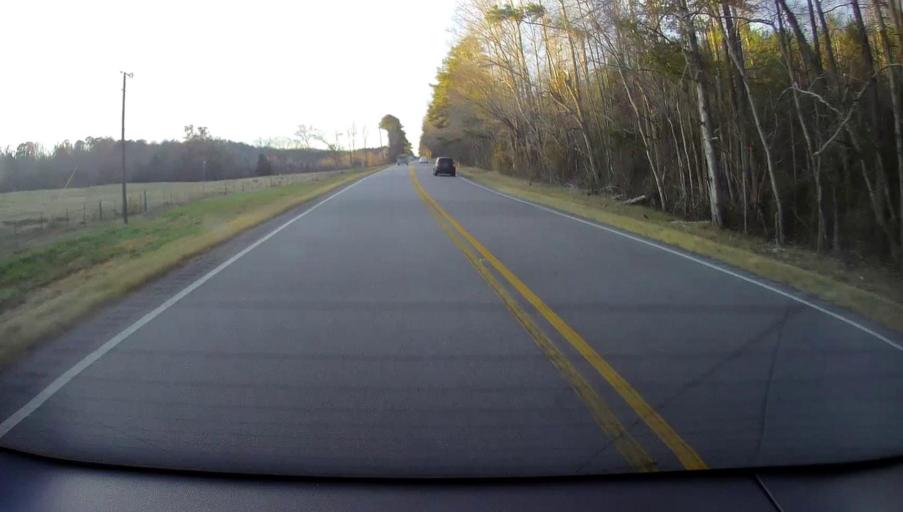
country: US
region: Alabama
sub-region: Saint Clair County
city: Steele
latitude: 34.0734
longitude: -86.3297
